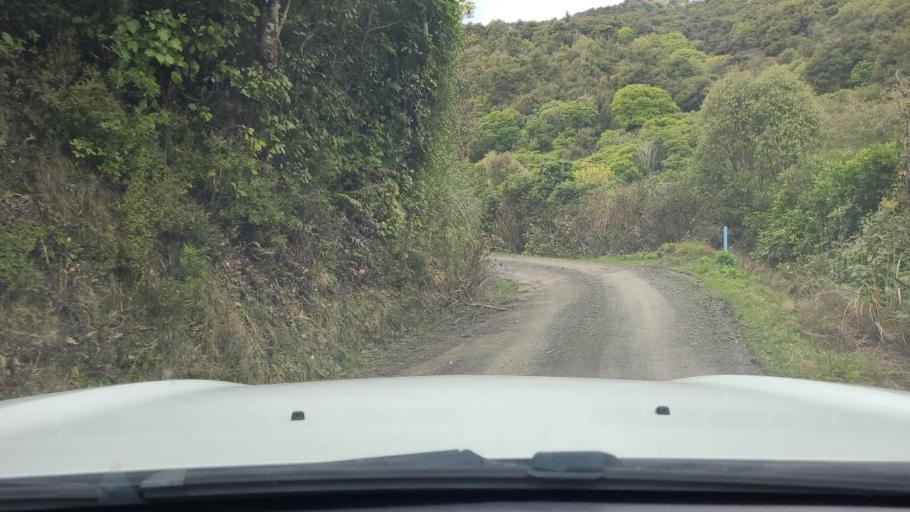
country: NZ
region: Wellington
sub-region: South Wairarapa District
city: Waipawa
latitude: -41.4116
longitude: 175.3623
